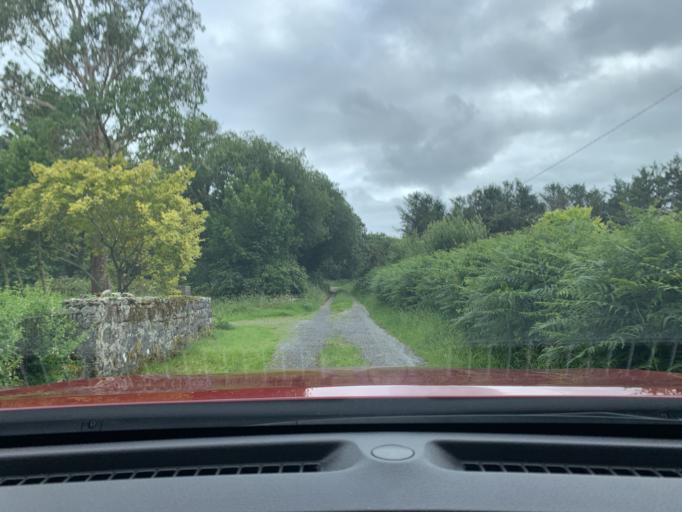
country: IE
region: Connaught
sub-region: County Leitrim
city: Kinlough
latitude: 54.4567
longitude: -8.3578
